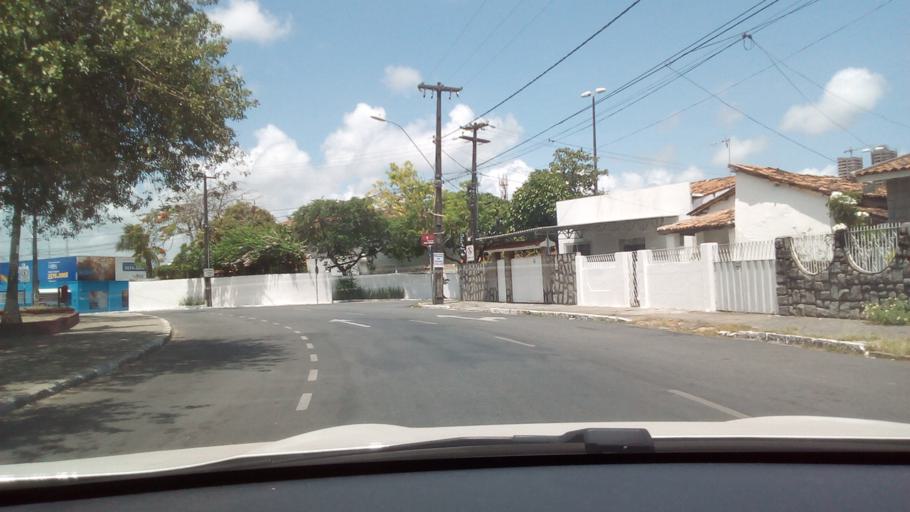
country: BR
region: Paraiba
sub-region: Joao Pessoa
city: Joao Pessoa
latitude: -7.1225
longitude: -34.8663
